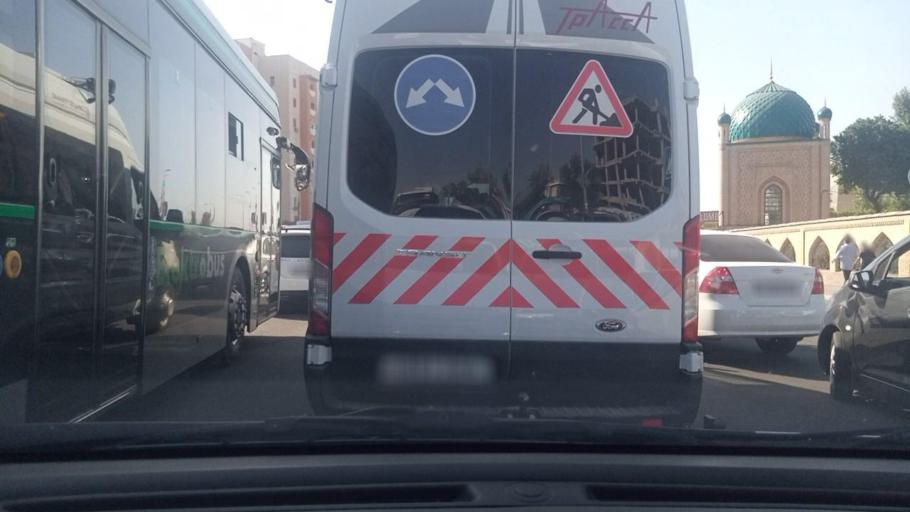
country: UZ
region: Toshkent Shahri
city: Bektemir
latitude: 41.2410
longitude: 69.3289
